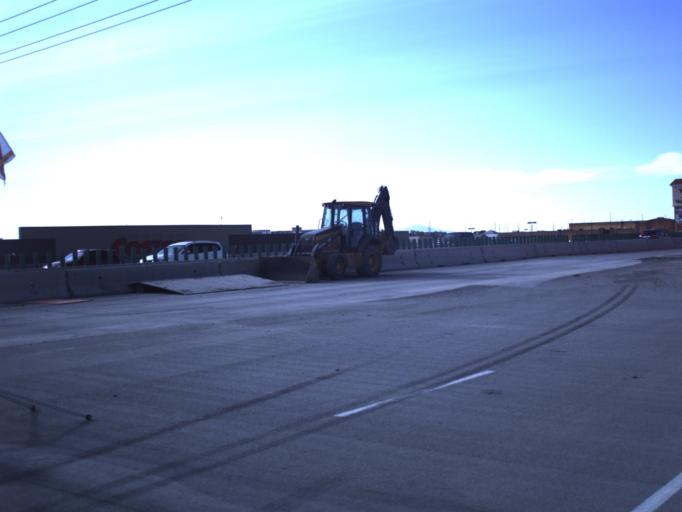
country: US
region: Utah
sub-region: Salt Lake County
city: Taylorsville
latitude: 40.6892
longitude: -111.9516
